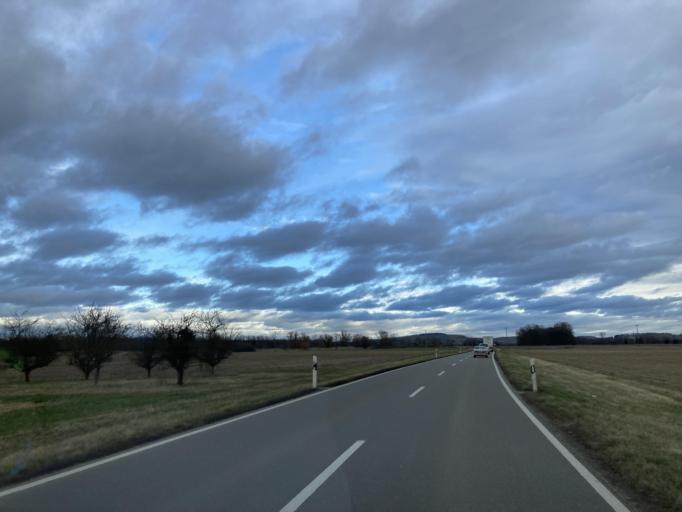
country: DE
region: Baden-Wuerttemberg
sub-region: Freiburg Region
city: Breisach am Rhein
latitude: 48.0592
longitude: 7.5938
